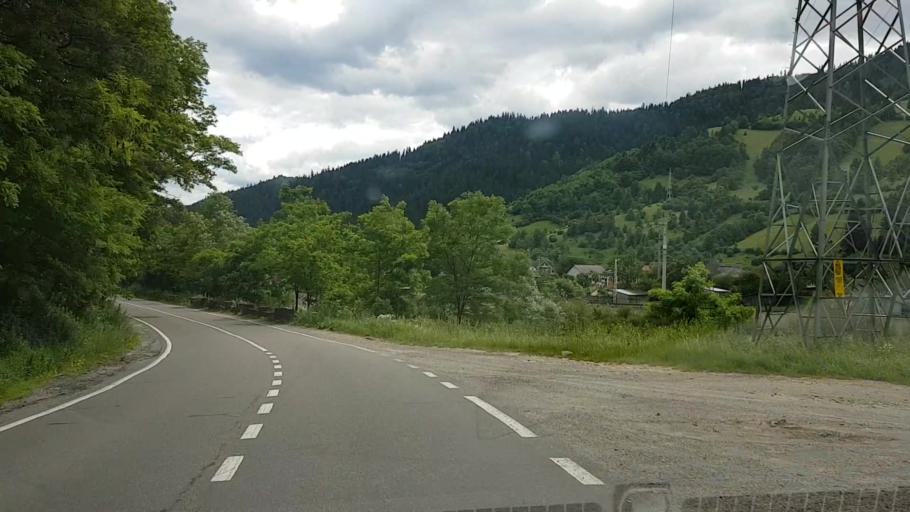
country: RO
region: Neamt
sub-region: Comuna Poiana Teiului
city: Poiana Teiului
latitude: 47.1228
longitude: 25.9077
